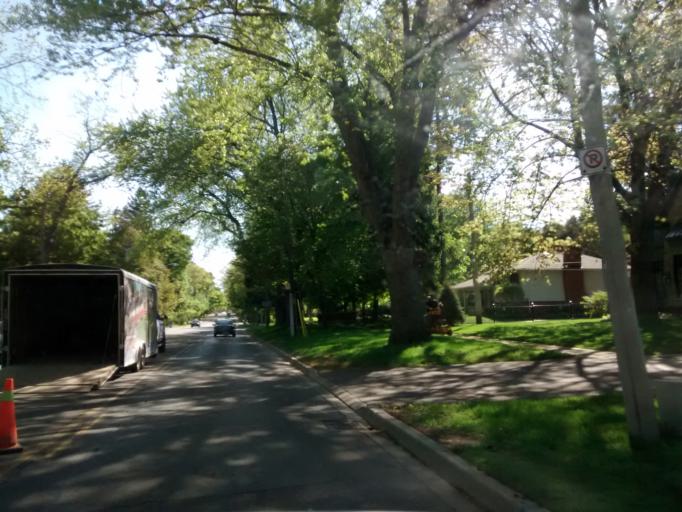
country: CA
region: Ontario
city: Burlington
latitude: 43.3632
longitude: -79.7404
